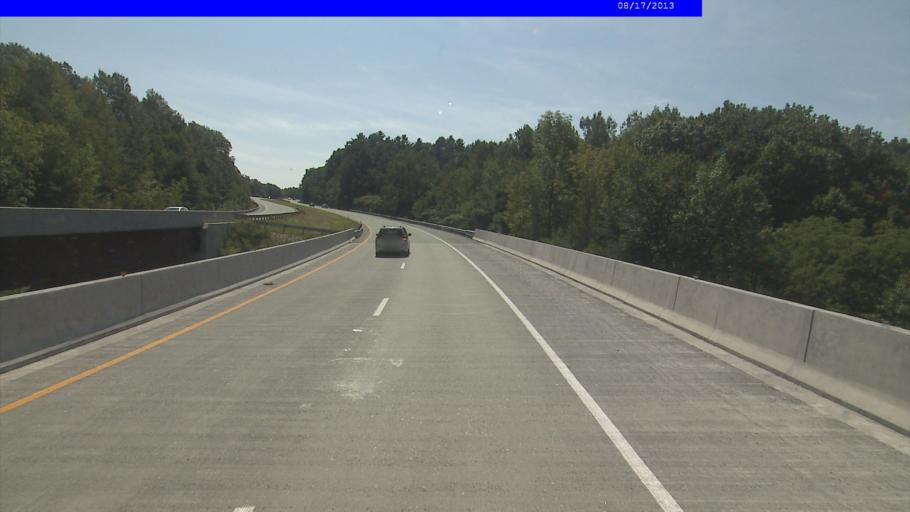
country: US
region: Vermont
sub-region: Windham County
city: Brattleboro
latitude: 42.8487
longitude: -72.5785
